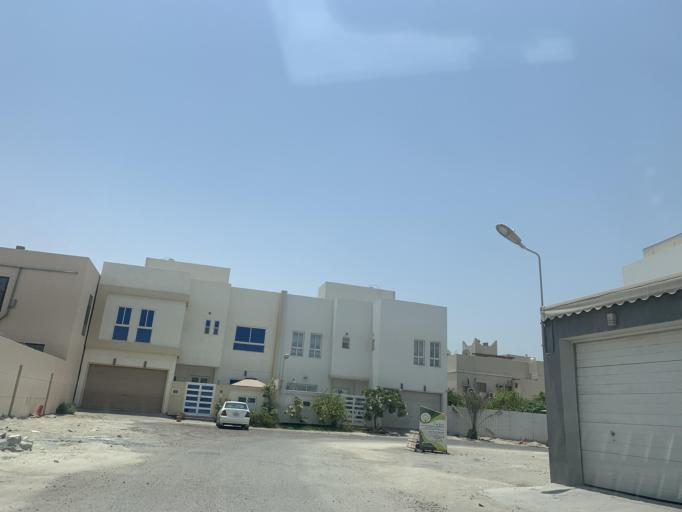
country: BH
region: Manama
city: Jidd Hafs
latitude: 26.2117
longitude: 50.4732
